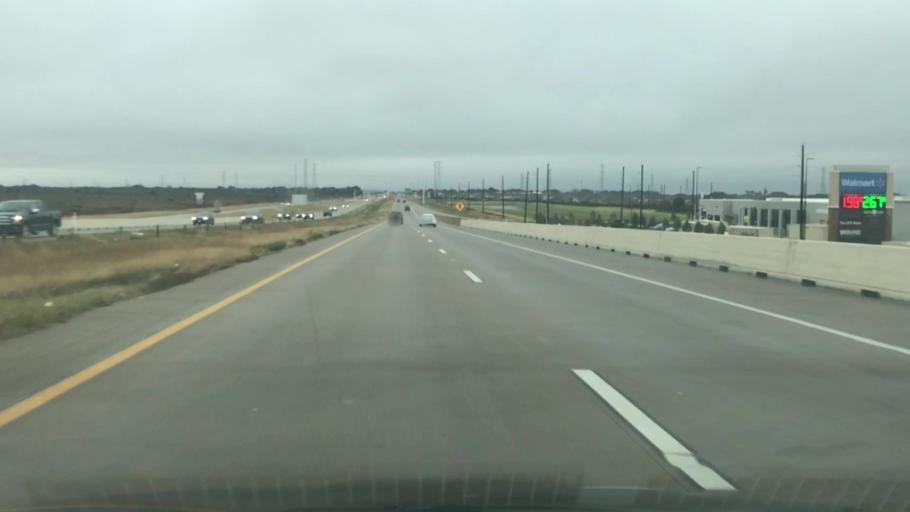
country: US
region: Texas
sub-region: Harris County
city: Katy
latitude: 29.8186
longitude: -95.7699
